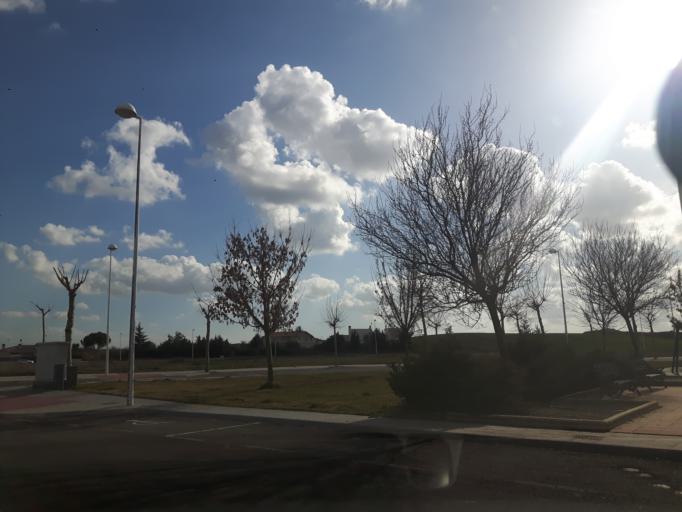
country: ES
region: Castille and Leon
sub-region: Provincia de Salamanca
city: Moriscos
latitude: 41.0068
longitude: -5.5901
